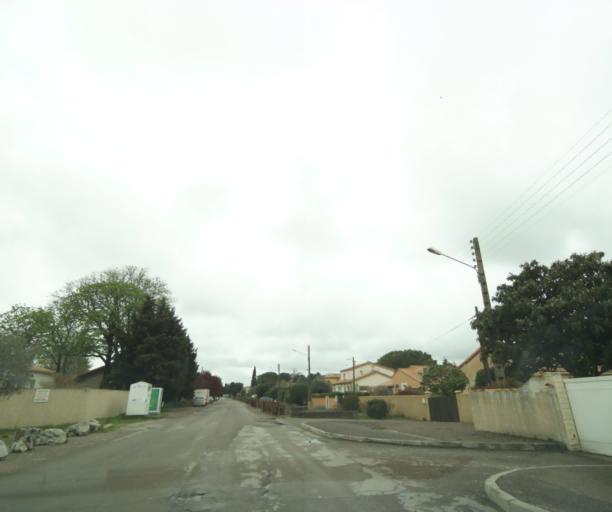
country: FR
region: Languedoc-Roussillon
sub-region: Departement de l'Herault
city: Cournonterral
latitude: 43.5579
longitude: 3.7124
